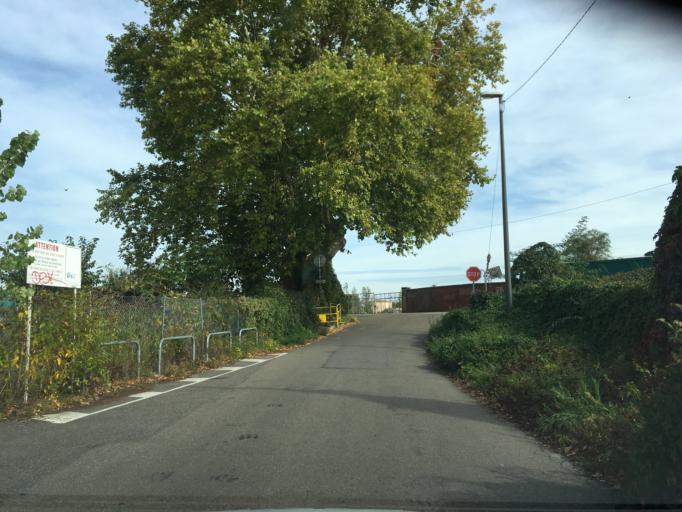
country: DE
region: Baden-Wuerttemberg
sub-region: Freiburg Region
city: Kehl
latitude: 48.5944
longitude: 7.7956
